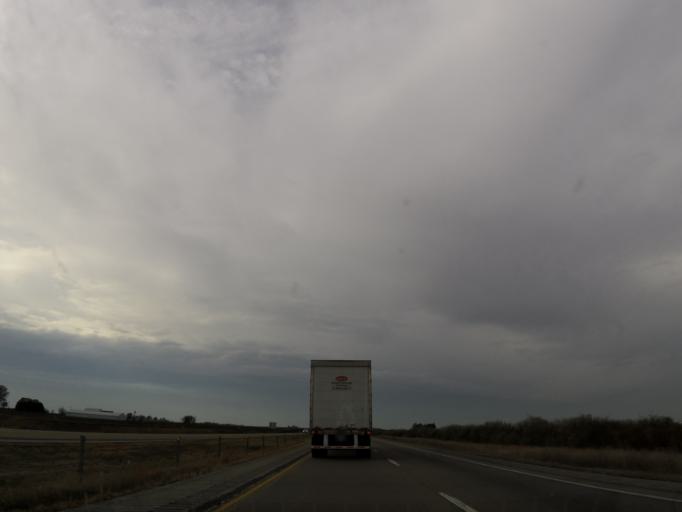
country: US
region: Iowa
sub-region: Scott County
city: Walcott
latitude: 41.6039
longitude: -90.7092
